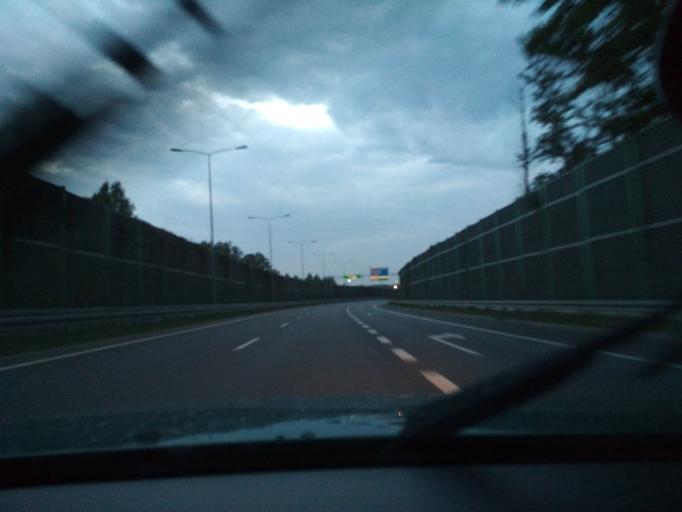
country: PL
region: Silesian Voivodeship
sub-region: Powiat gliwicki
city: Przyszowice
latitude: 50.2812
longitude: 18.7366
